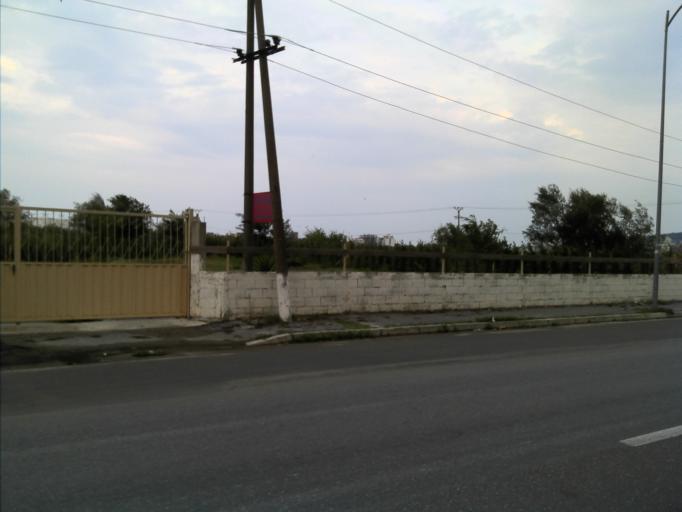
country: AL
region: Lezhe
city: Shengjin
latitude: 41.8005
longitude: 19.6166
